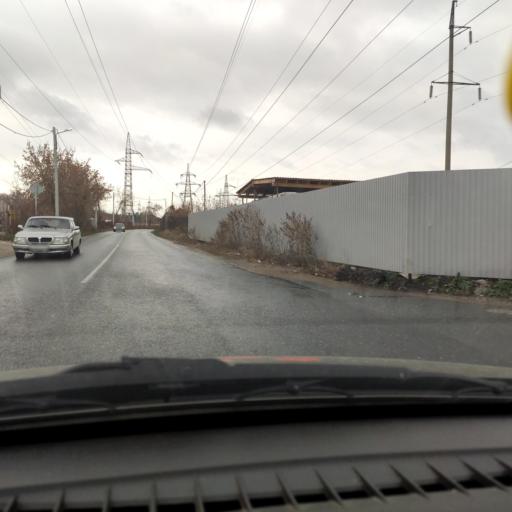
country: RU
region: Samara
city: Zhigulevsk
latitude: 53.5184
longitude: 49.4822
